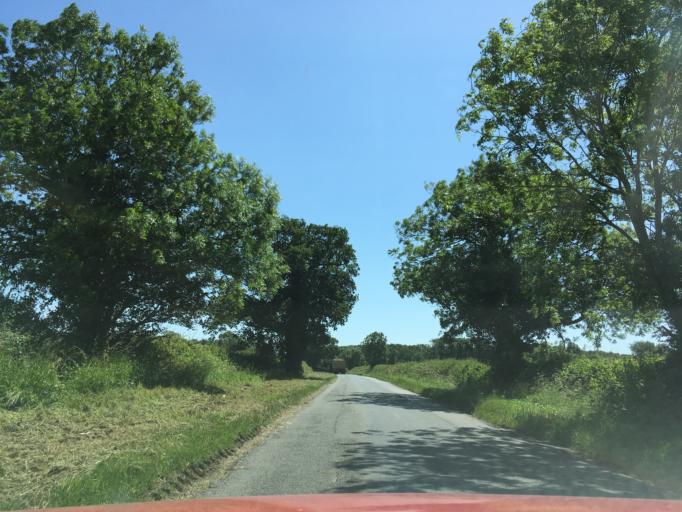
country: GB
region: England
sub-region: Northamptonshire
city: Deanshanger
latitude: 52.0079
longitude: -0.8932
